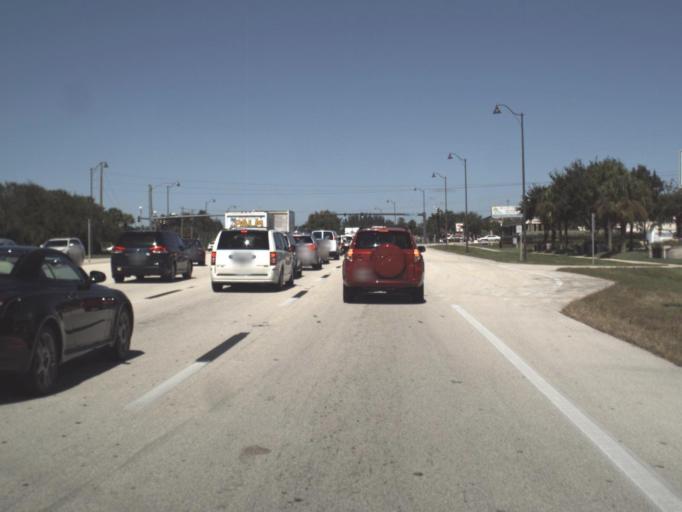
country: US
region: Florida
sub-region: Lee County
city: Bonita Springs
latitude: 26.3787
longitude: -81.8078
